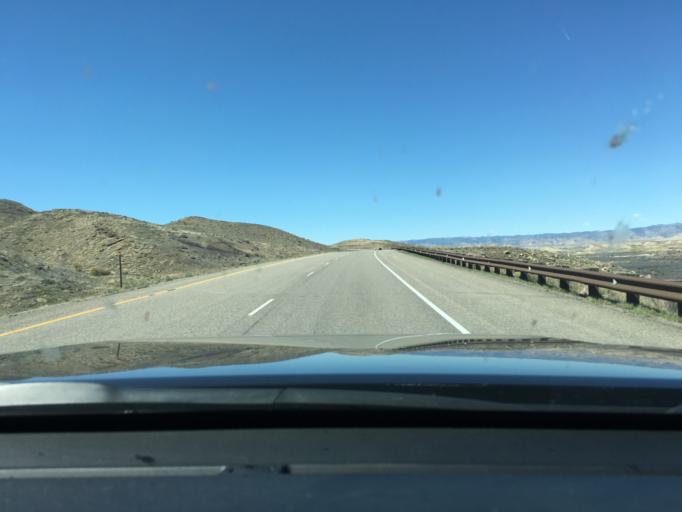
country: US
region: Colorado
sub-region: Mesa County
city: Loma
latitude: 39.2262
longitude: -108.8966
